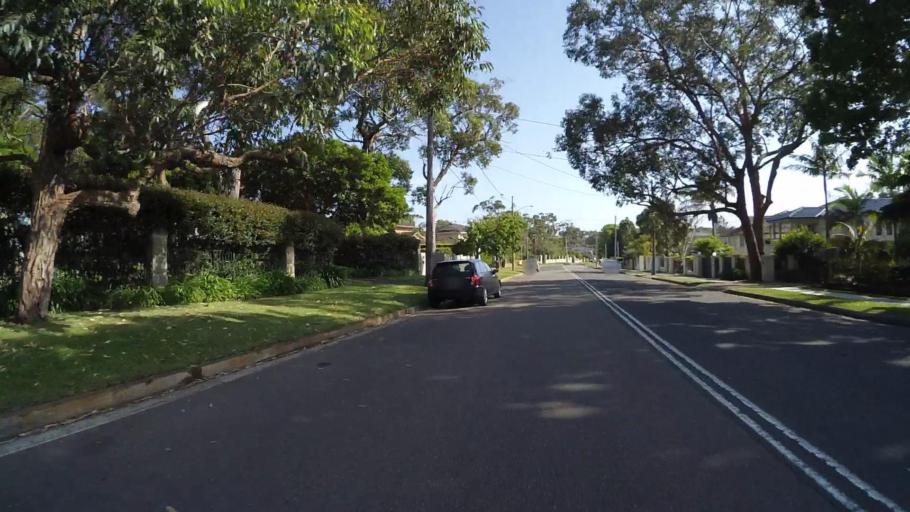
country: AU
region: New South Wales
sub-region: Sutherland Shire
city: Dolans Bay
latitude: -34.0659
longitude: 151.1372
